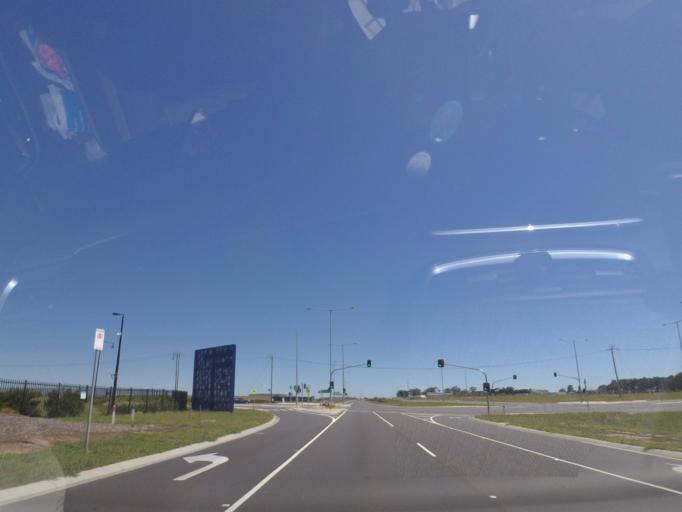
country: AU
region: Victoria
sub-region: Hume
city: Tullamarine
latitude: -37.6931
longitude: 144.8661
